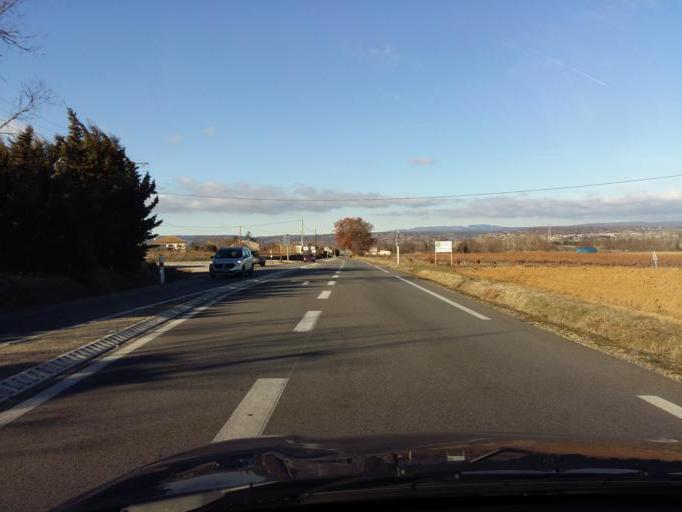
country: FR
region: Rhone-Alpes
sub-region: Departement de l'Ardeche
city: Saint-Just-d'Ardeche
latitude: 44.2752
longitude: 4.6261
